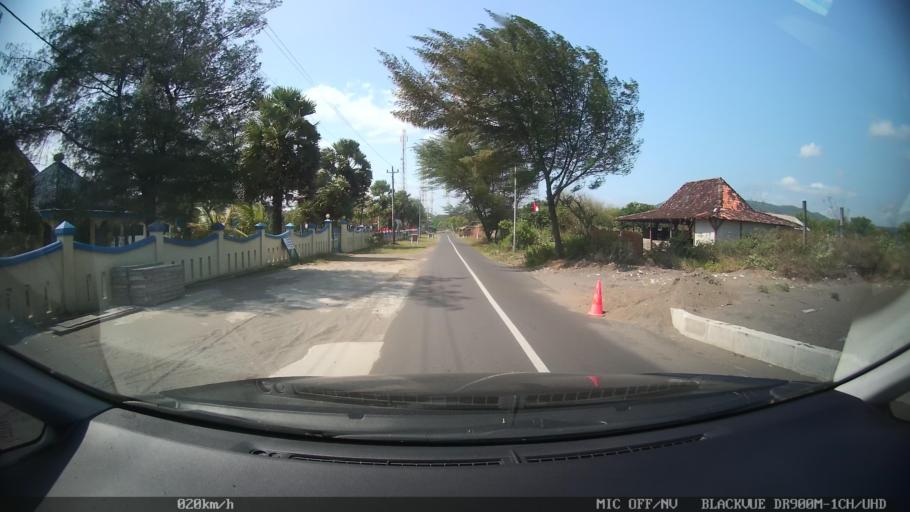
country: ID
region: Daerah Istimewa Yogyakarta
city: Bambanglipuro
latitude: -8.0110
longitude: 110.2948
